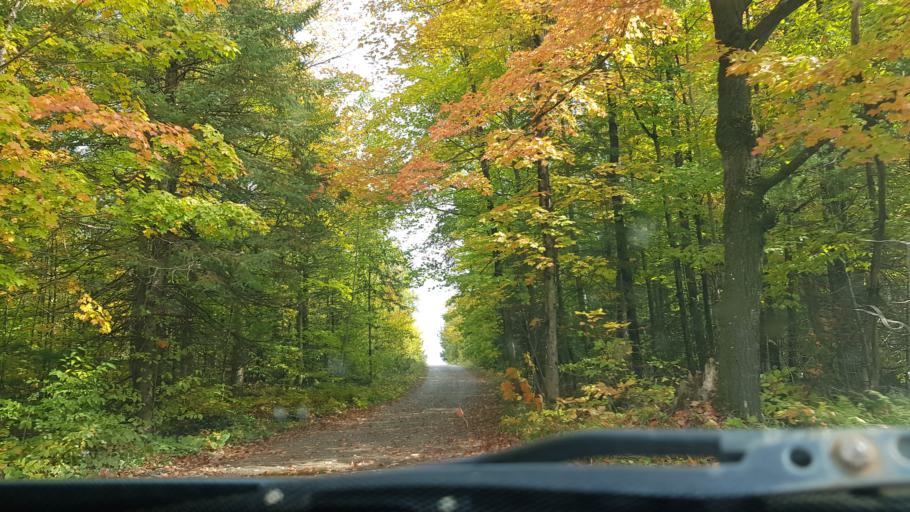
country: CA
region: Ontario
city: Orillia
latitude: 44.6831
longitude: -79.0591
